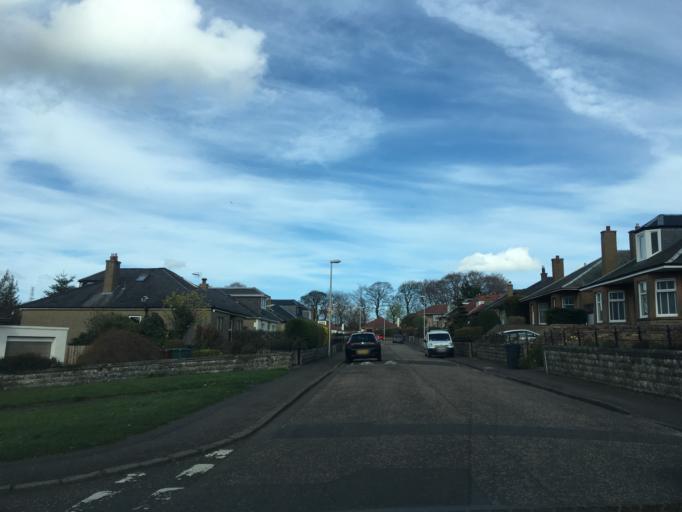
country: GB
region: Scotland
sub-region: Edinburgh
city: Edinburgh
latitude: 55.9053
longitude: -3.2066
